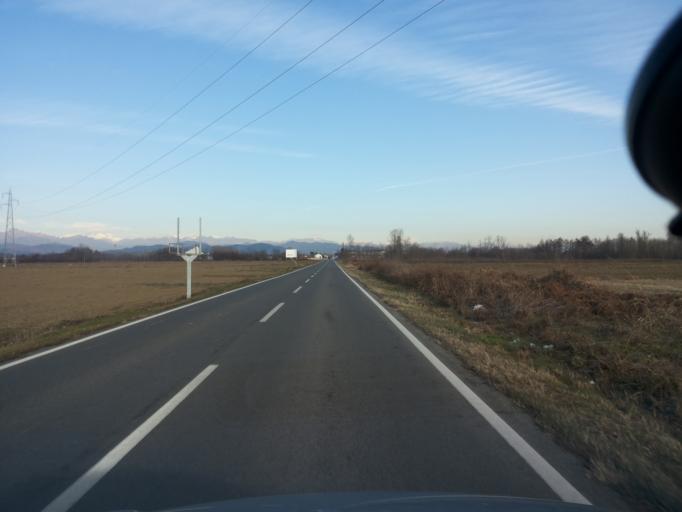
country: IT
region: Piedmont
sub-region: Provincia di Vercelli
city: Lenta
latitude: 45.5429
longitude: 8.3851
